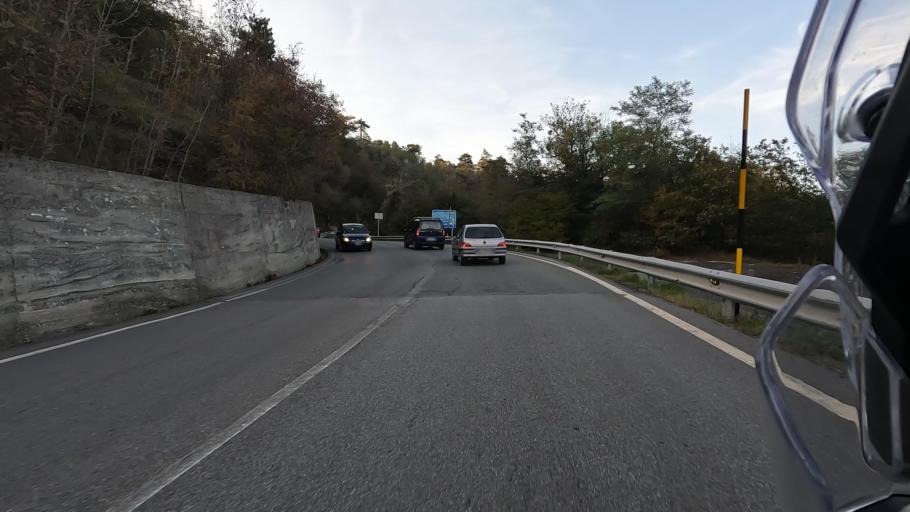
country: IT
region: Liguria
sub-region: Provincia di Savona
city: Osteria dei Cacciatori-Stella
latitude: 44.4265
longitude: 8.4740
